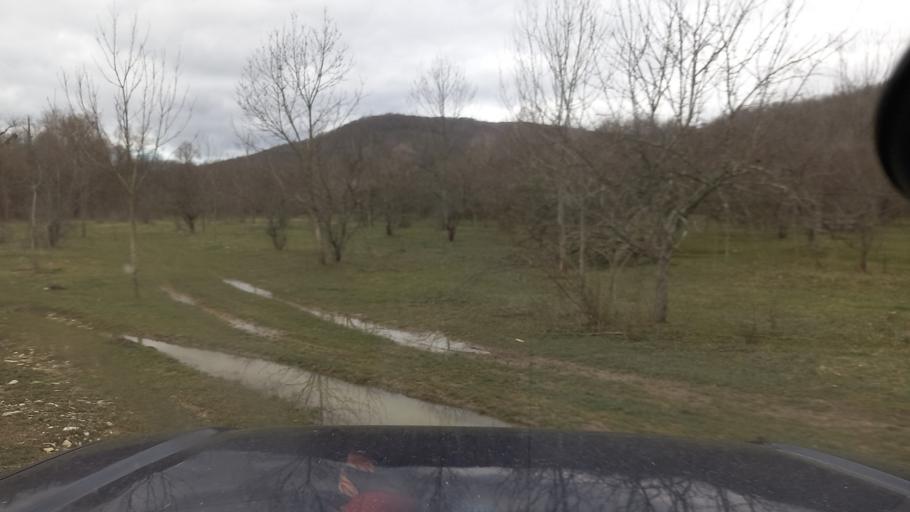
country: RU
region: Krasnodarskiy
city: Pshada
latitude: 44.4858
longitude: 38.4067
